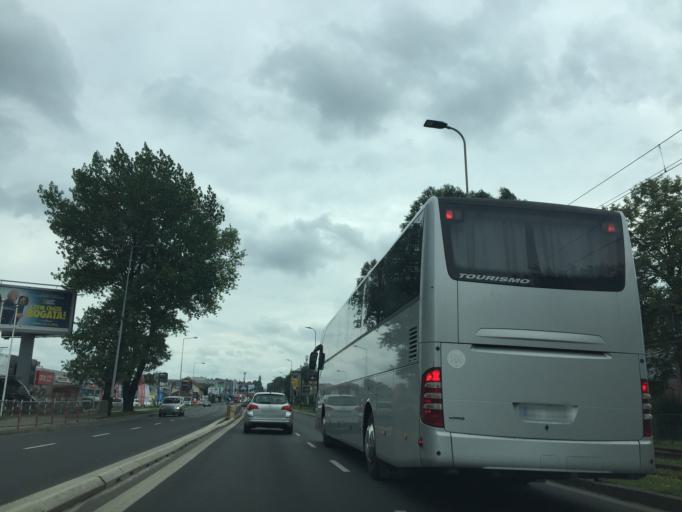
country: PL
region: Lesser Poland Voivodeship
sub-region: Krakow
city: Krakow
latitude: 50.0210
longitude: 19.9322
